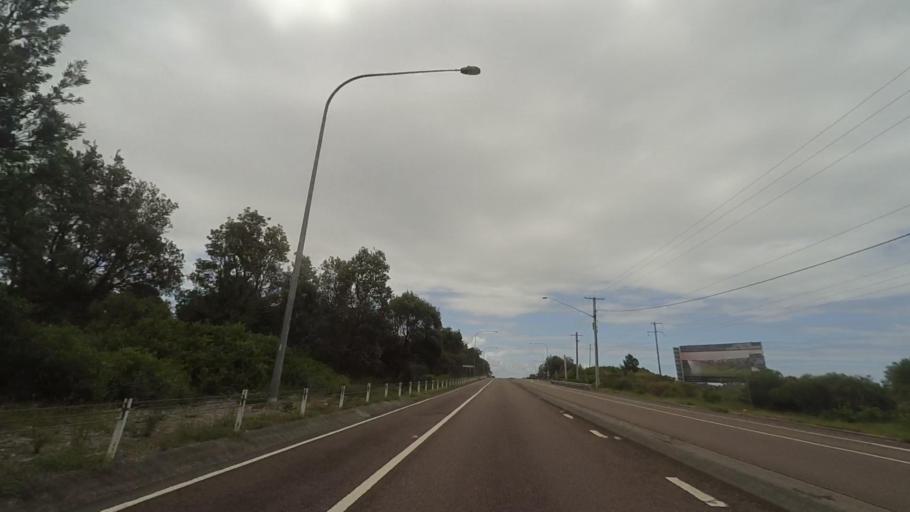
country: AU
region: New South Wales
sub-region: Wyong Shire
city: The Entrance
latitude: -33.3124
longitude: 151.5197
